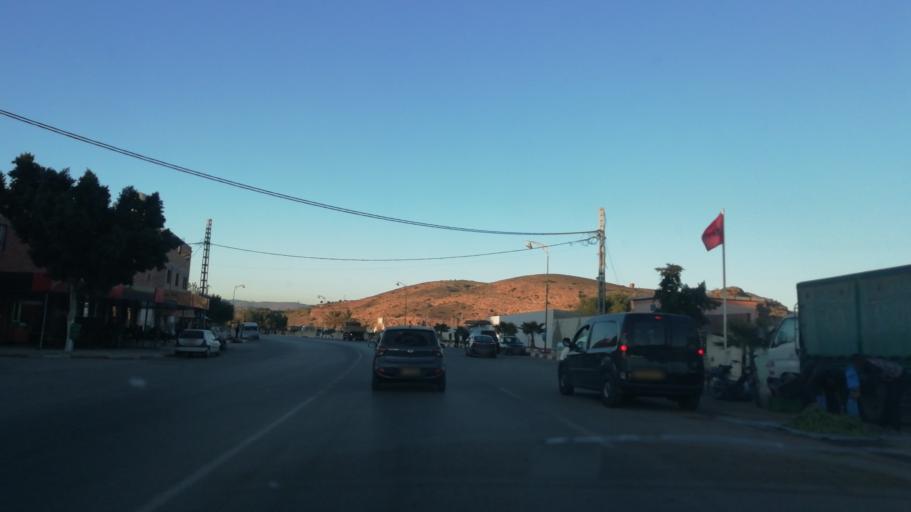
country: DZ
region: Tlemcen
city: Nedroma
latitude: 34.8937
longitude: -1.6364
